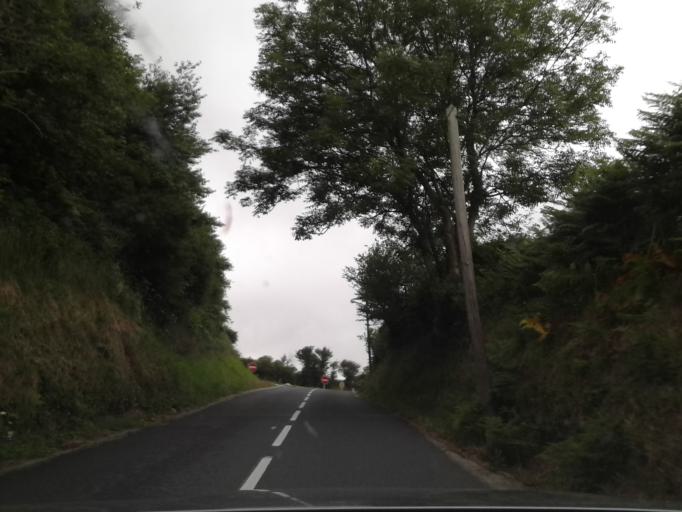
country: FR
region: Lower Normandy
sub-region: Departement de la Manche
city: Beaumont-Hague
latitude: 49.6823
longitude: -1.8553
